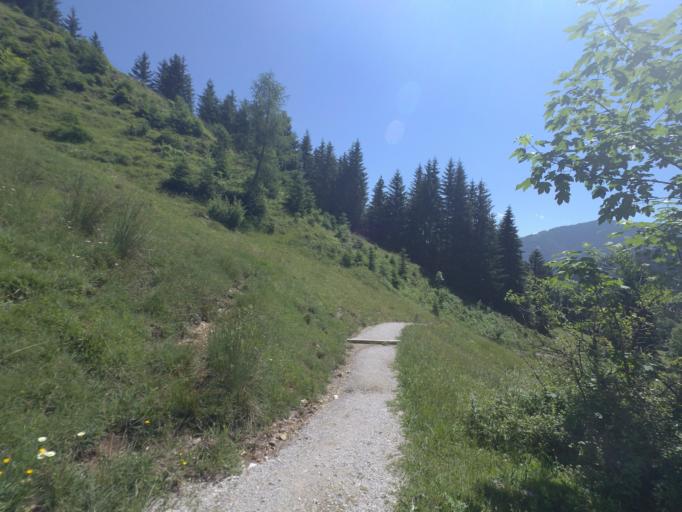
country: AT
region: Salzburg
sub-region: Politischer Bezirk Zell am See
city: Leogang
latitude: 47.4560
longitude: 12.7537
